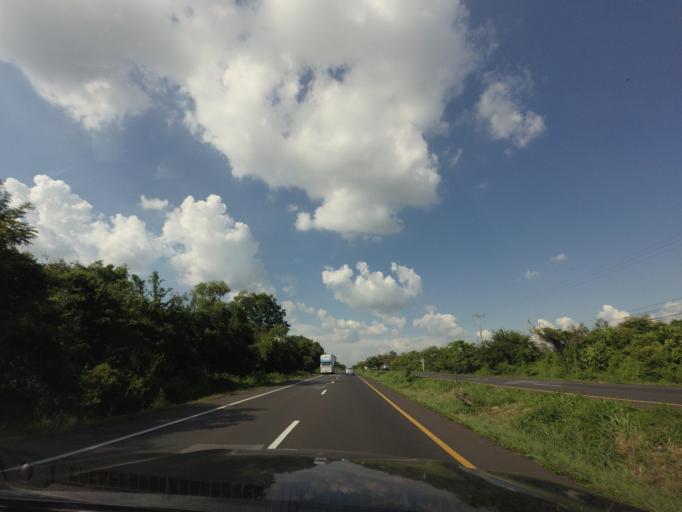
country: TH
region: Nakhon Ratchasima
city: Bua Lai
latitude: 15.6894
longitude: 102.5797
